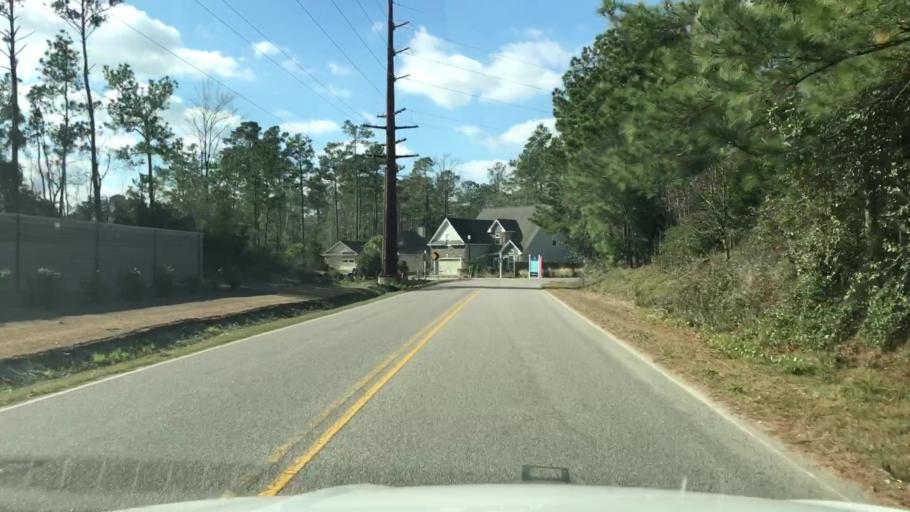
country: US
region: South Carolina
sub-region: Horry County
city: Socastee
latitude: 33.6581
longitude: -78.9980
